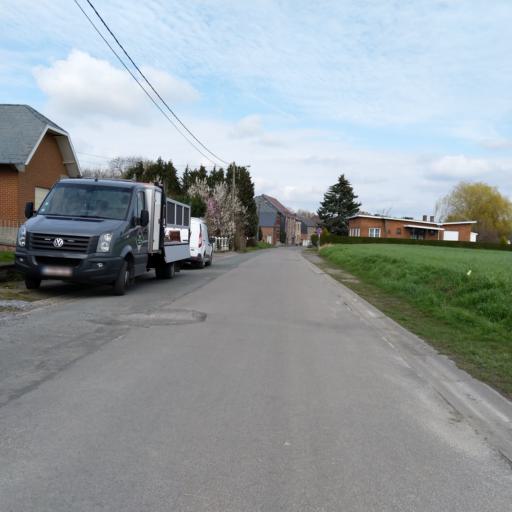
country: BE
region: Wallonia
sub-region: Province du Hainaut
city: Soignies
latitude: 50.5656
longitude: 4.0538
